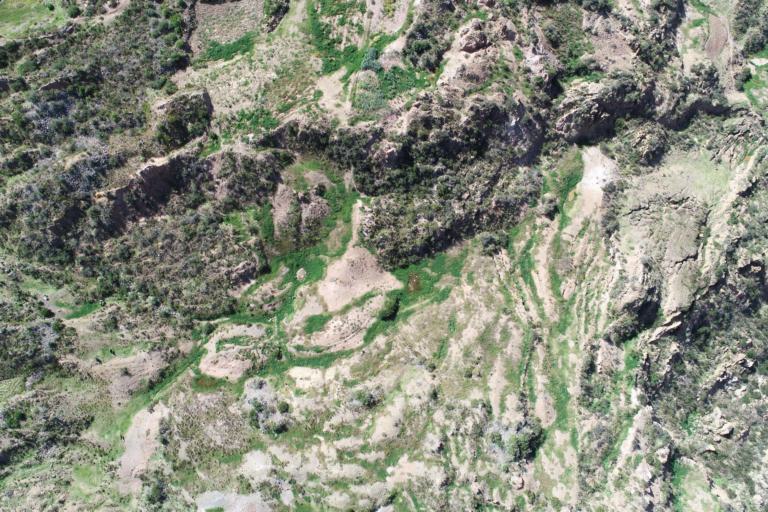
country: BO
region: La Paz
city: La Paz
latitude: -16.5590
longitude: -67.9872
